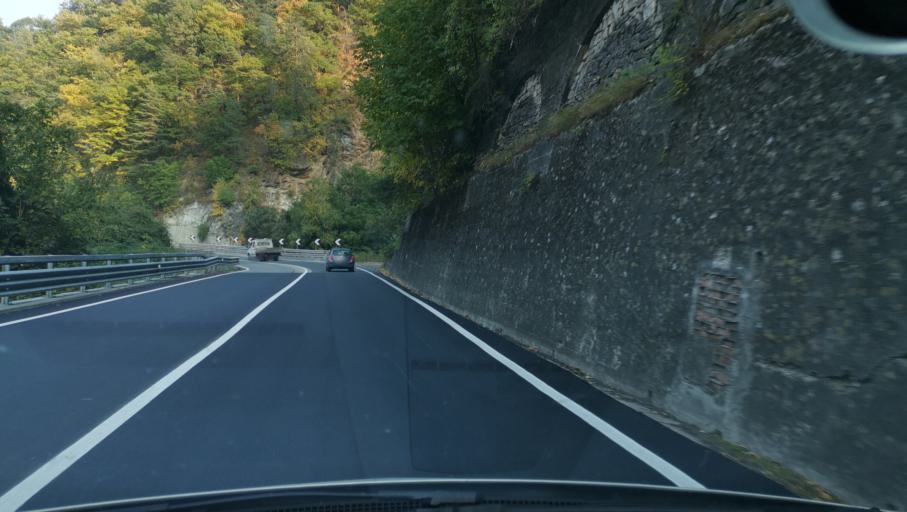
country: IT
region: Piedmont
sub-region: Provincia di Torino
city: Chiomonte
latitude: 45.1119
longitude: 6.9682
